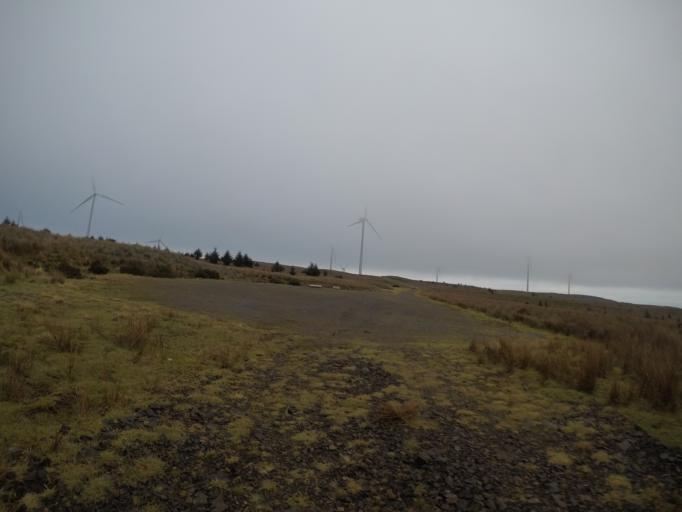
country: GB
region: Scotland
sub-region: North Ayrshire
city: Fairlie
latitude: 55.7364
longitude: -4.7888
